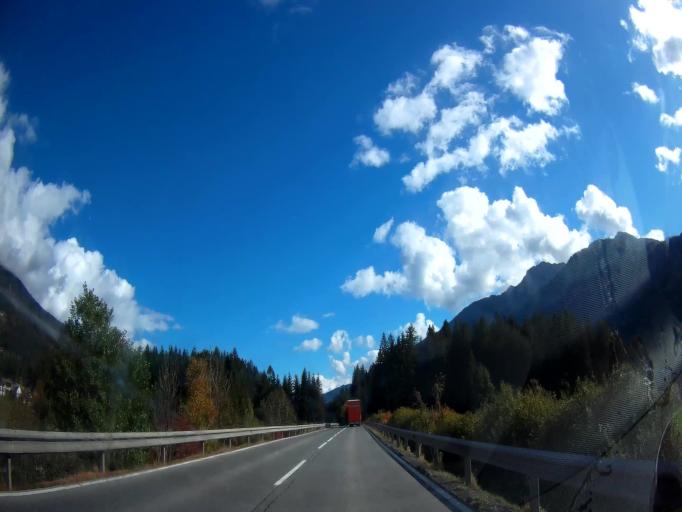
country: AT
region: Carinthia
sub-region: Politischer Bezirk Spittal an der Drau
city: Irschen
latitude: 46.7417
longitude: 13.0235
